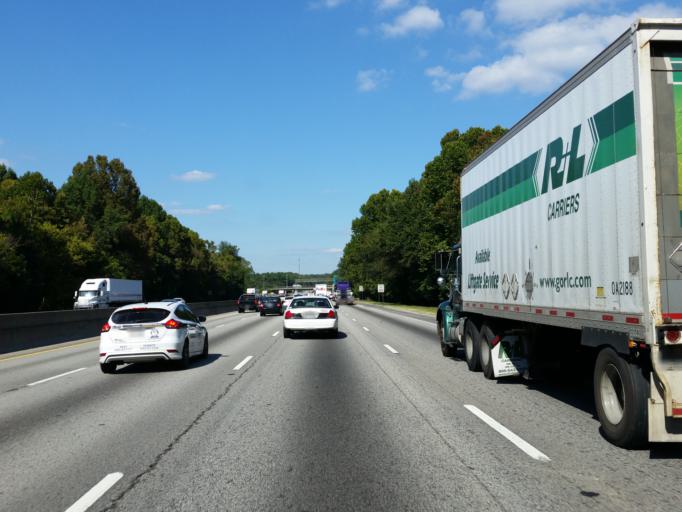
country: US
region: Georgia
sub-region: Clayton County
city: Forest Park
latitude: 33.6469
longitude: -84.3710
